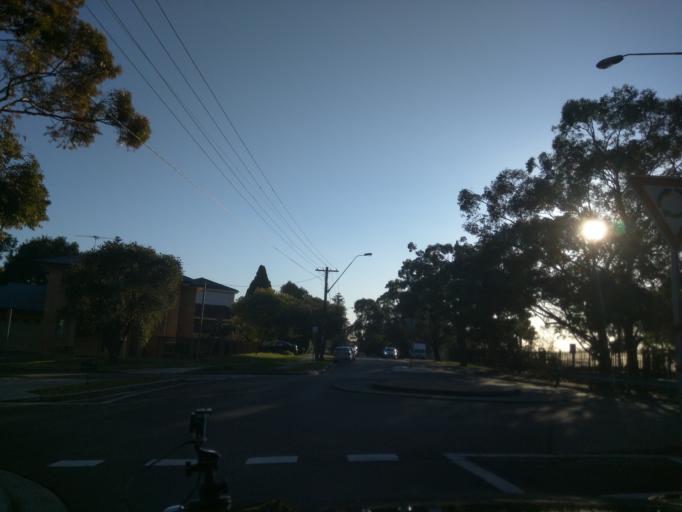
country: AU
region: New South Wales
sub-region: Sutherland Shire
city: Jannali
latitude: -34.0267
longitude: 151.0602
